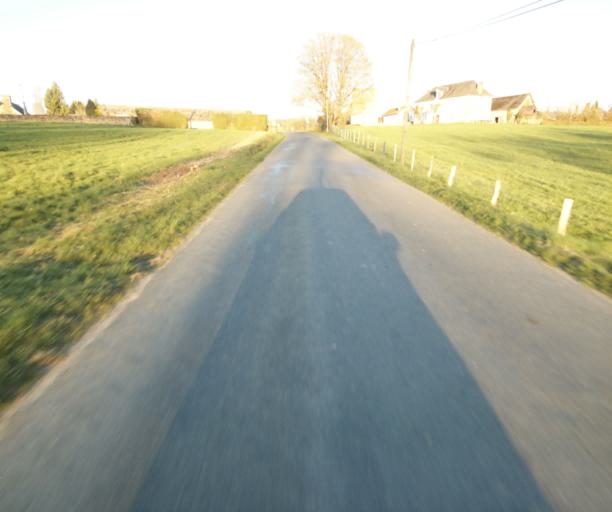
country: FR
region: Limousin
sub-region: Departement de la Correze
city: Saint-Clement
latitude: 45.3222
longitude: 1.6681
